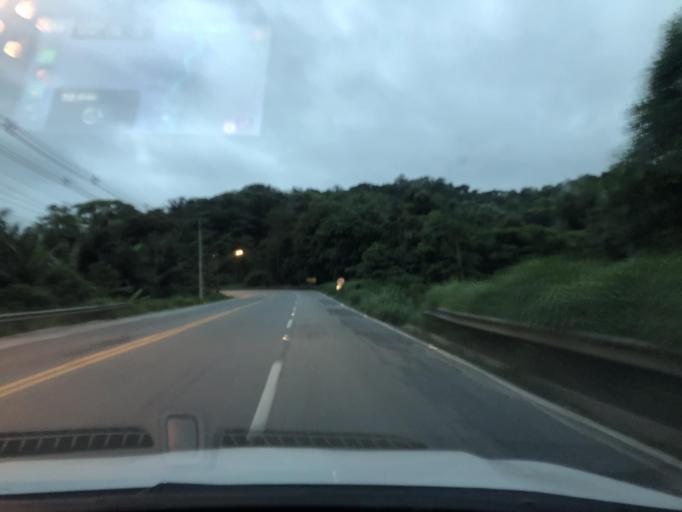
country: BR
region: Santa Catarina
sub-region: Pomerode
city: Pomerode
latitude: -26.7550
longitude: -49.0715
